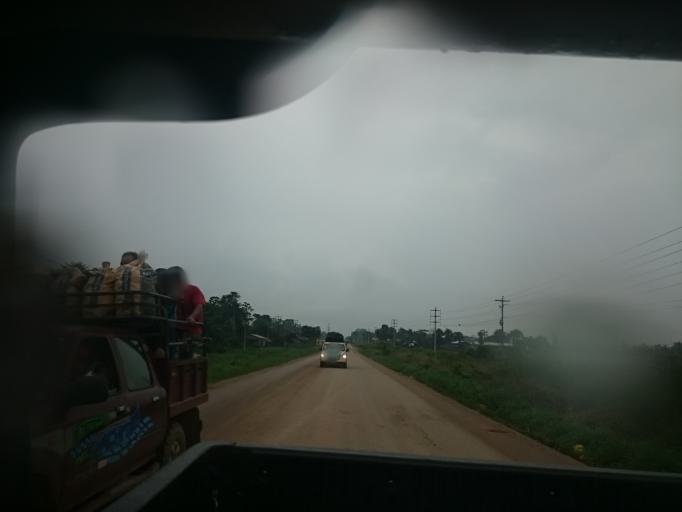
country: PE
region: Ucayali
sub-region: Provincia de Coronel Portillo
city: Puerto Callao
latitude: -8.4026
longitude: -74.6219
